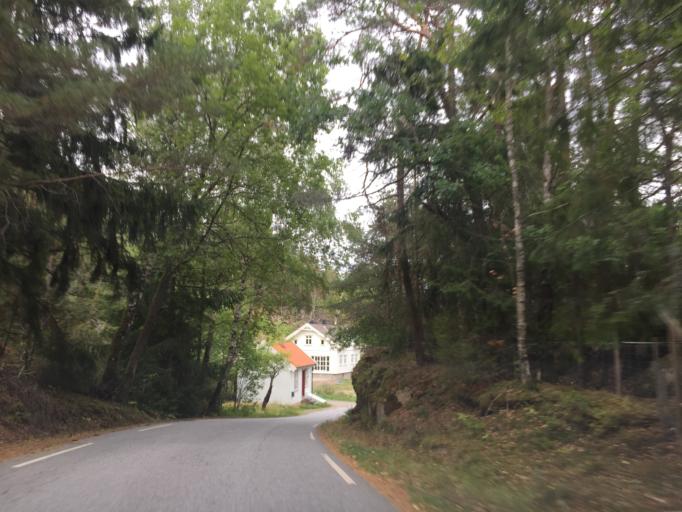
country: NO
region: Ostfold
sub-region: Hvaler
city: Skjaerhalden
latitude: 59.0589
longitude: 11.0612
